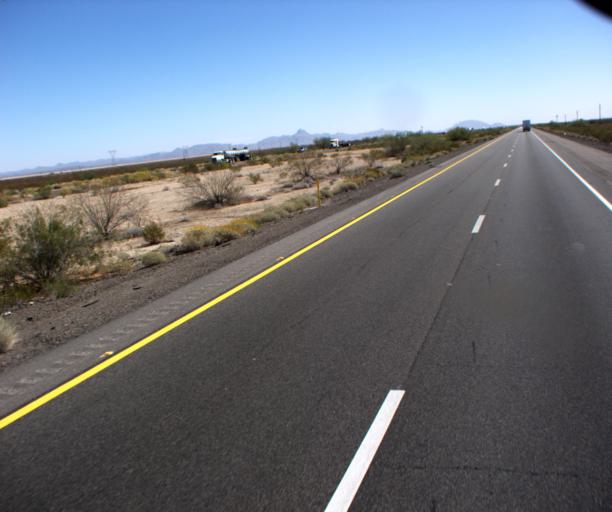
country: US
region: Arizona
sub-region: La Paz County
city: Salome
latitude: 33.5748
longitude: -113.3934
